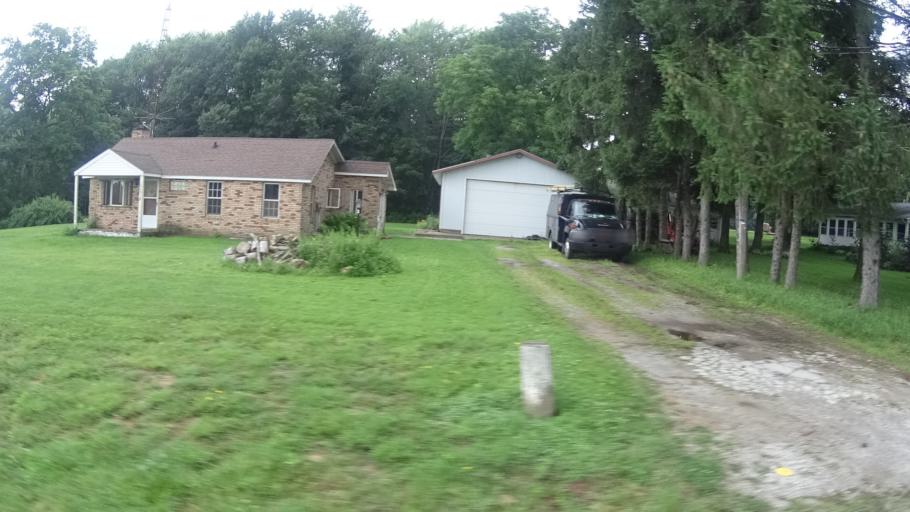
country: US
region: Ohio
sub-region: Erie County
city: Huron
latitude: 41.3217
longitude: -82.4817
